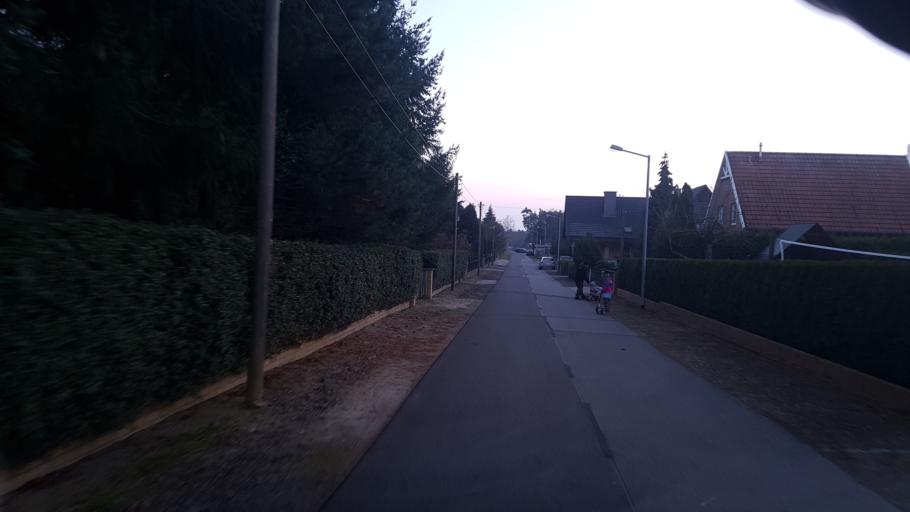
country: DE
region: Brandenburg
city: Lauchhammer
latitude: 51.5142
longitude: 13.7168
